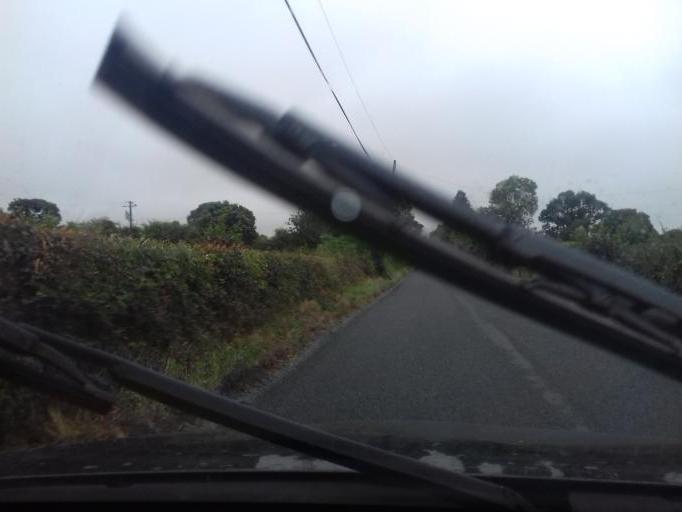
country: IE
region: Leinster
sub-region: Kilkenny
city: Graiguenamanagh
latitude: 52.6111
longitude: -6.9369
